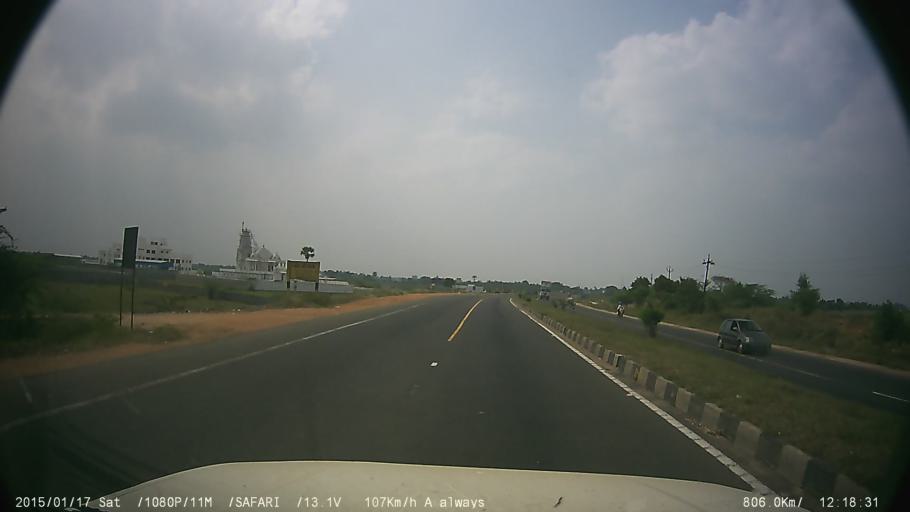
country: IN
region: Tamil Nadu
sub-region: Kancheepuram
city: Wallajahbad
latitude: 12.9060
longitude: 79.8274
